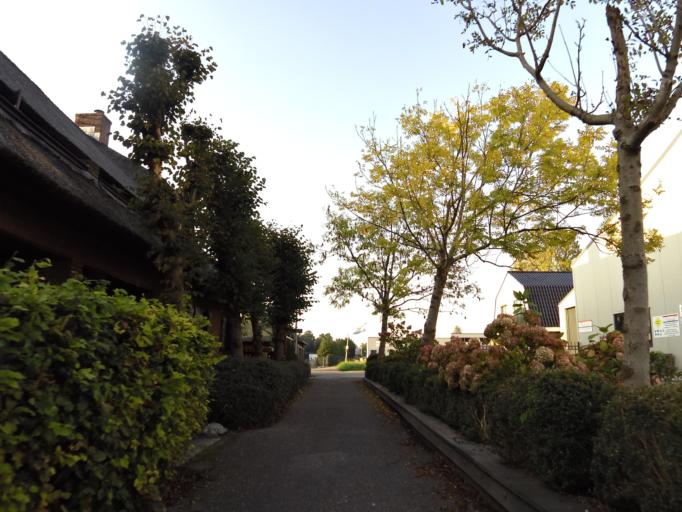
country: NL
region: South Holland
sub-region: Gemeente Kaag en Braassem
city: Oude Wetering
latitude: 52.1708
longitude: 4.6362
